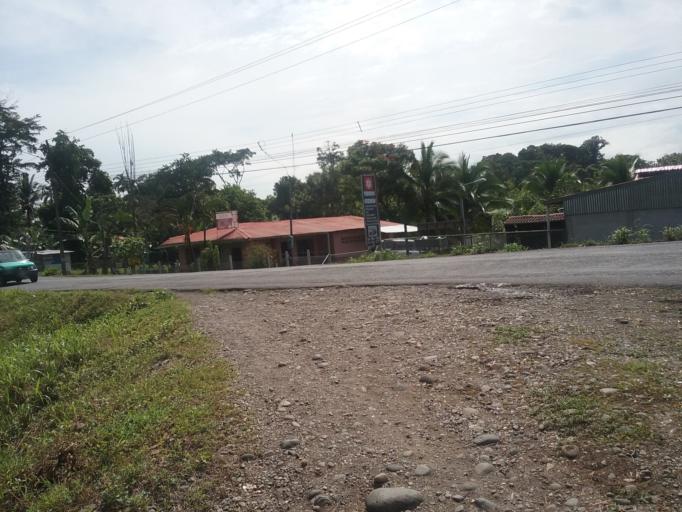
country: CR
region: Limon
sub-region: Canton de Pococi
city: Guapiles
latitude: 10.3202
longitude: -83.9094
